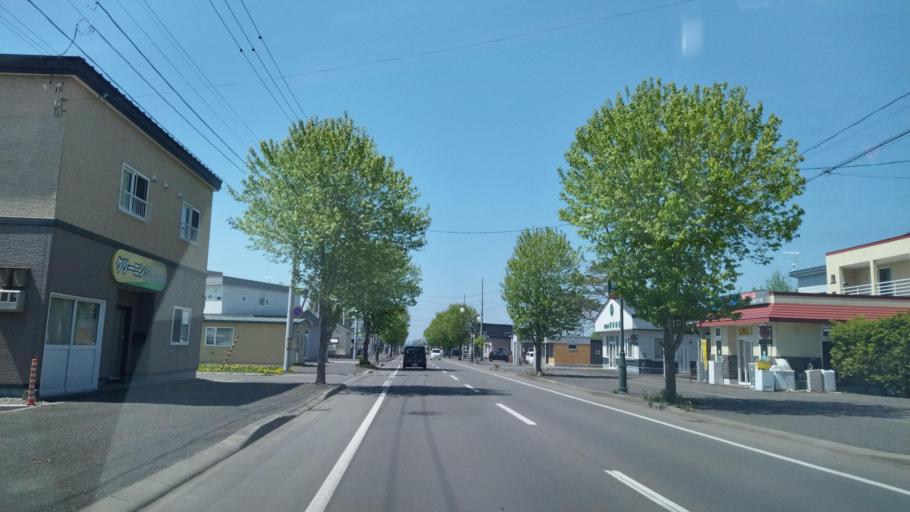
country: JP
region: Hokkaido
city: Otofuke
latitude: 43.2336
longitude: 143.2918
